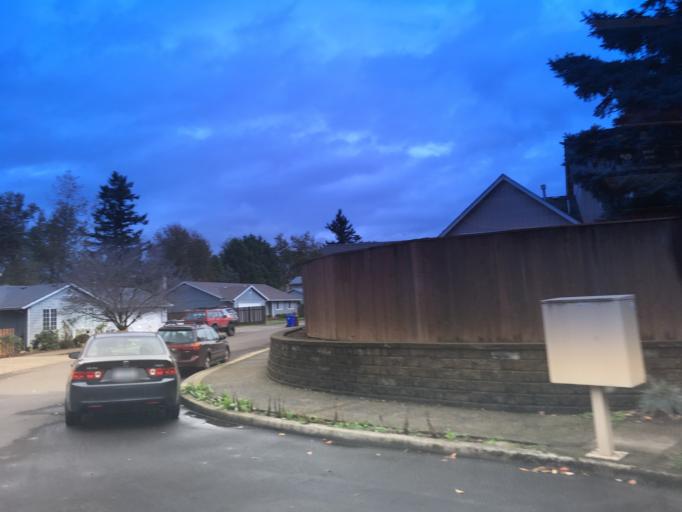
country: US
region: Oregon
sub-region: Multnomah County
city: Fairview
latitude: 45.5402
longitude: -122.4313
